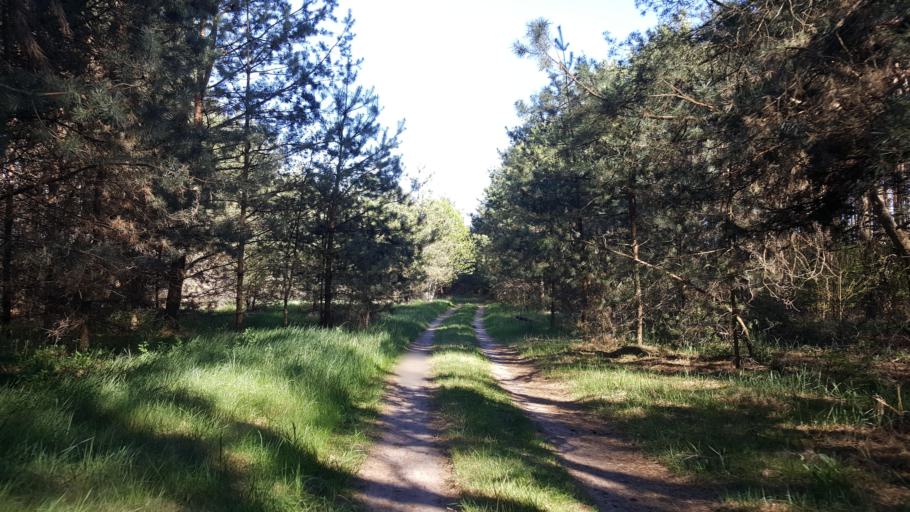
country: BY
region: Brest
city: Kamyanyets
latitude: 52.4383
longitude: 23.8806
